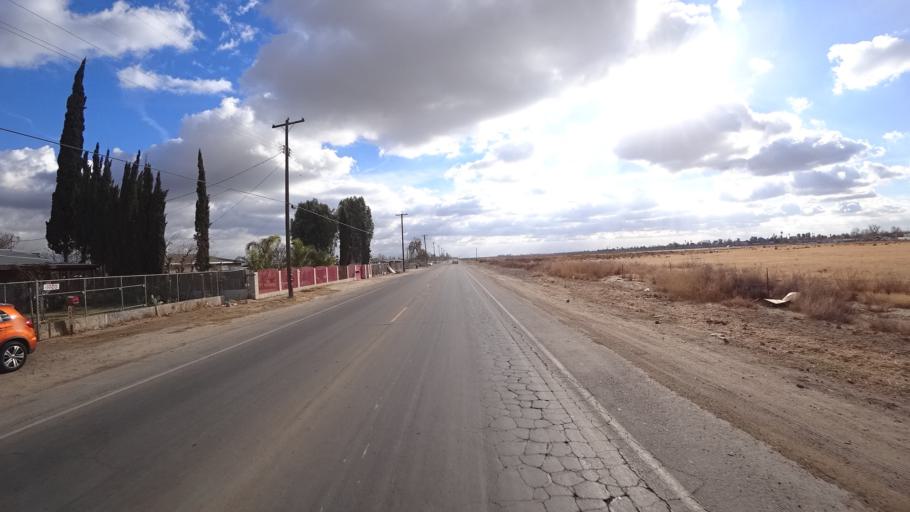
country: US
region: California
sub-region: Kern County
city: Greenfield
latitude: 35.3132
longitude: -118.9855
